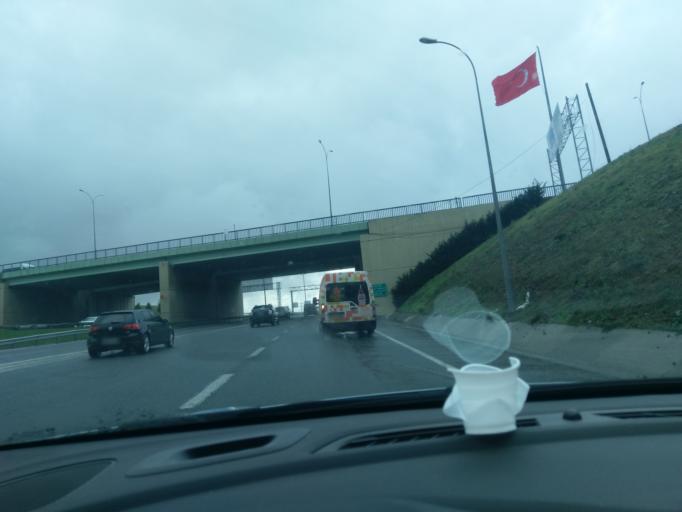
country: TR
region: Istanbul
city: Sisli
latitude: 41.0956
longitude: 28.9633
